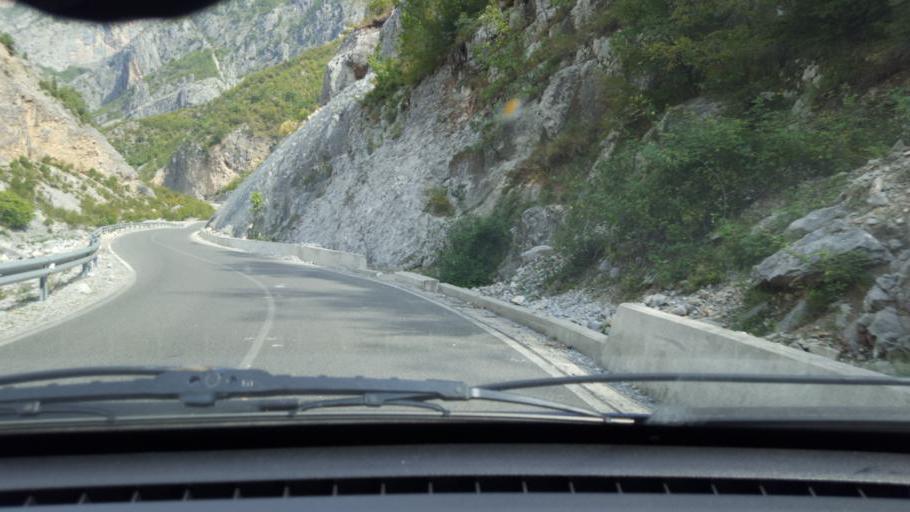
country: AL
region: Shkoder
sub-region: Rrethi i Malesia e Madhe
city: Kastrat
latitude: 42.4732
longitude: 19.5727
